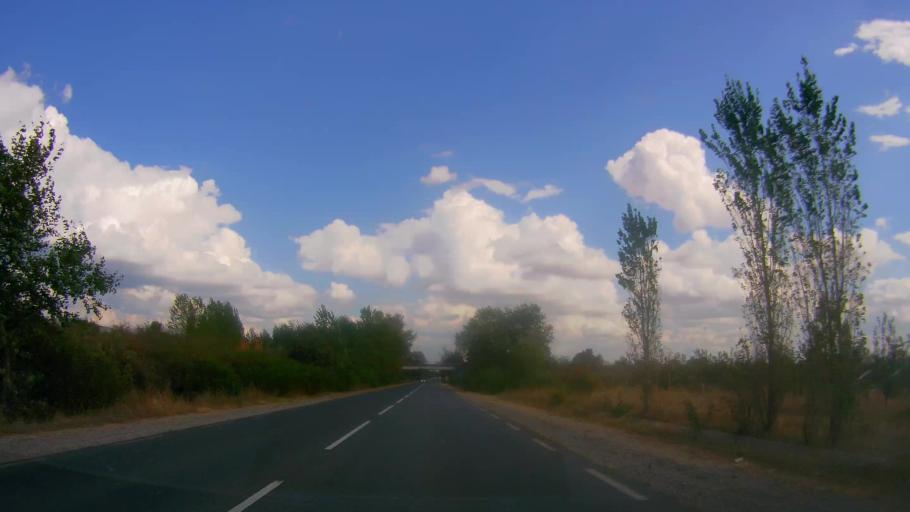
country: BG
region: Sliven
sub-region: Obshtina Sliven
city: Sliven
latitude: 42.6349
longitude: 26.2138
